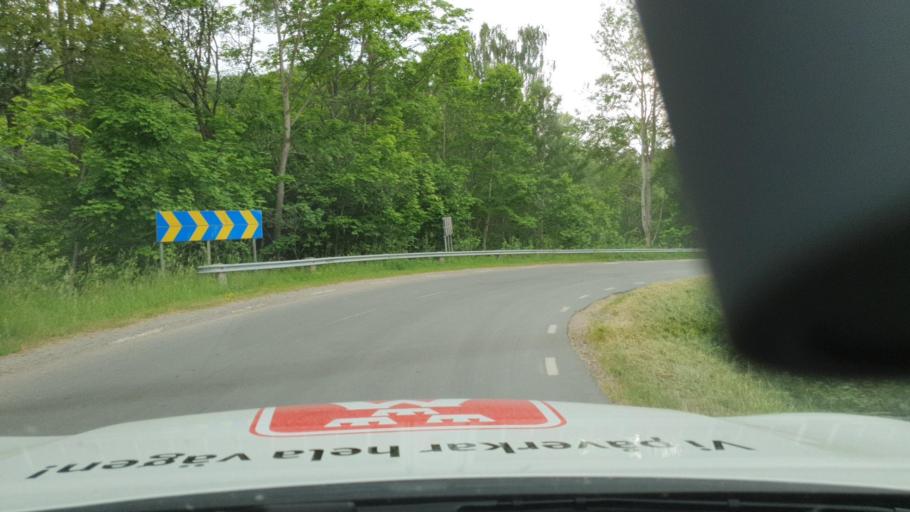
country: SE
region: Vaestra Goetaland
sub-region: Hjo Kommun
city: Hjo
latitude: 58.1764
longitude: 14.1934
